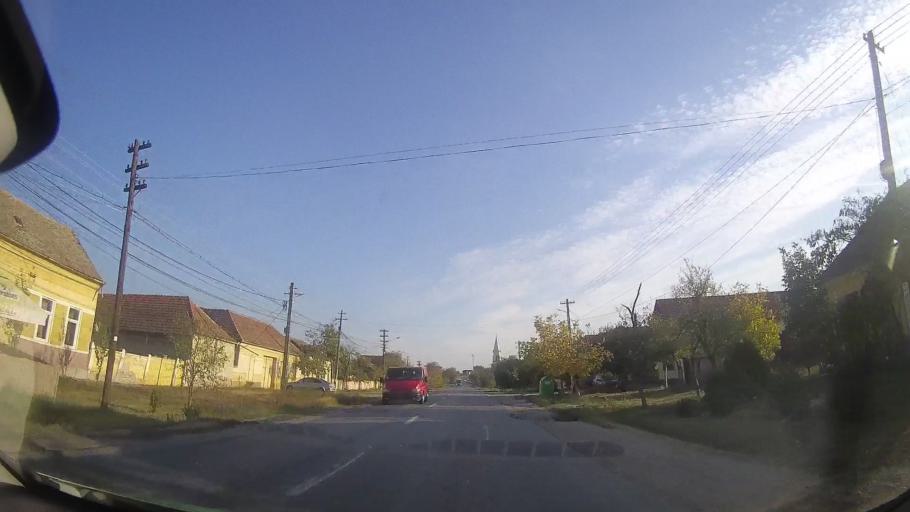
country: RO
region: Timis
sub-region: Comuna Fibis
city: Fibis
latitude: 45.9771
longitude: 21.4249
